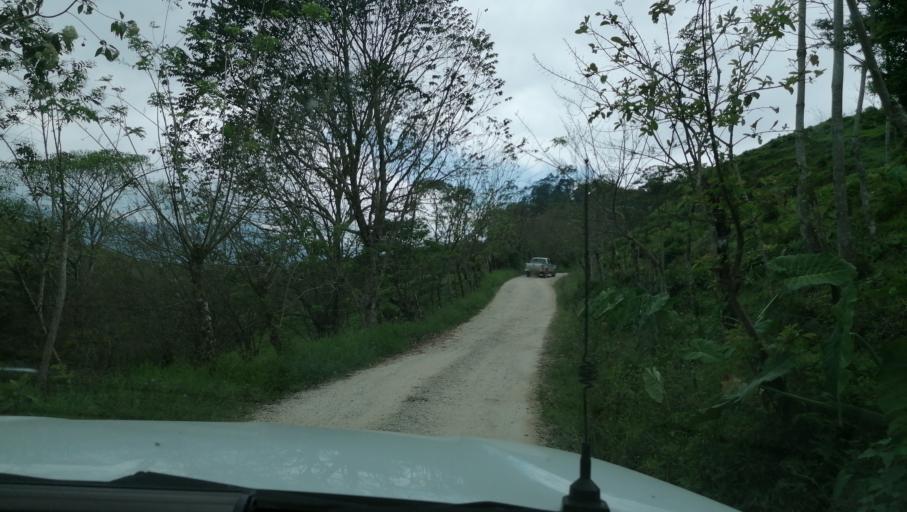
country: MX
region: Chiapas
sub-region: Ocotepec
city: San Pablo Huacano
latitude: 17.2713
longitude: -93.2427
